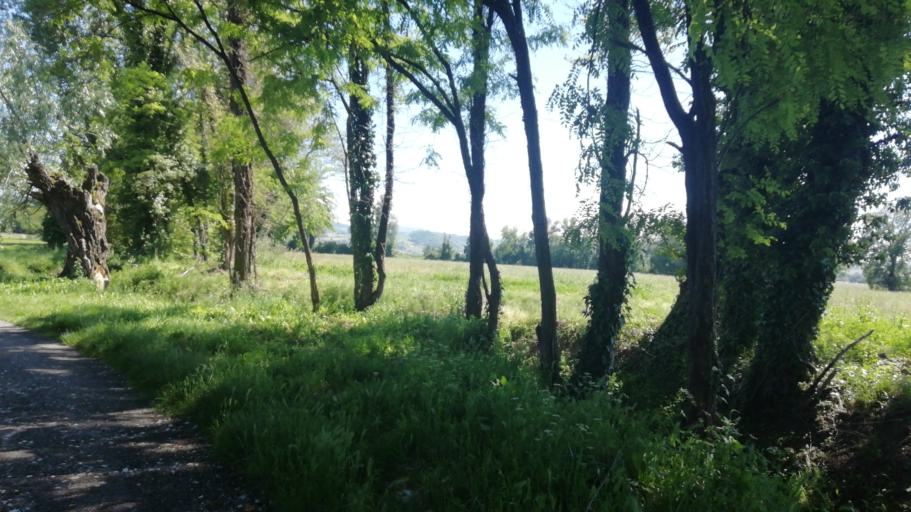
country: IT
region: Emilia-Romagna
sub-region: Provincia di Piacenza
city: Borgonovo Valtidone
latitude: 44.9920
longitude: 9.4571
